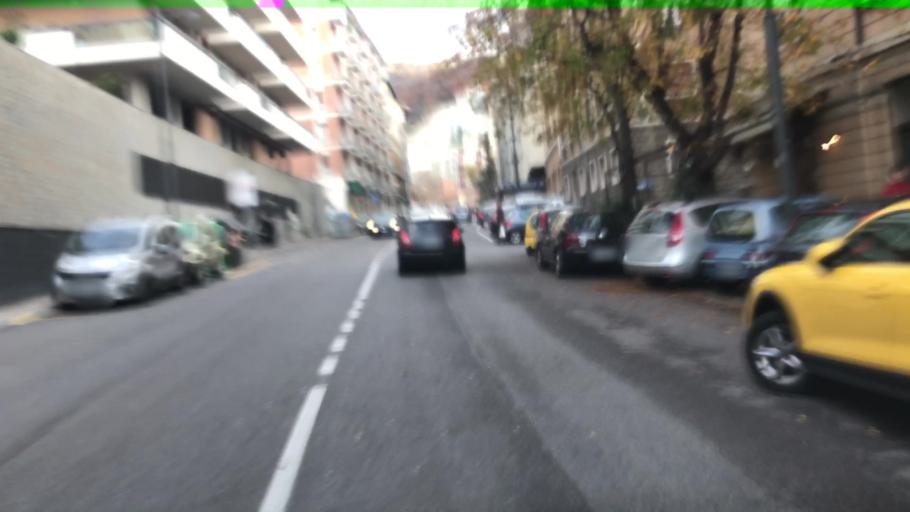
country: IT
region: Friuli Venezia Giulia
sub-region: Provincia di Trieste
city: Trieste
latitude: 45.6583
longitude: 13.7895
